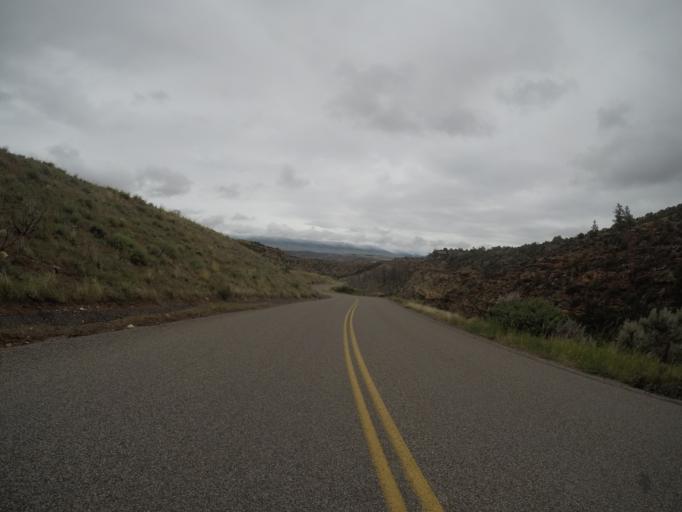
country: US
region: Wyoming
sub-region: Big Horn County
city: Lovell
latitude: 45.1090
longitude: -108.2394
